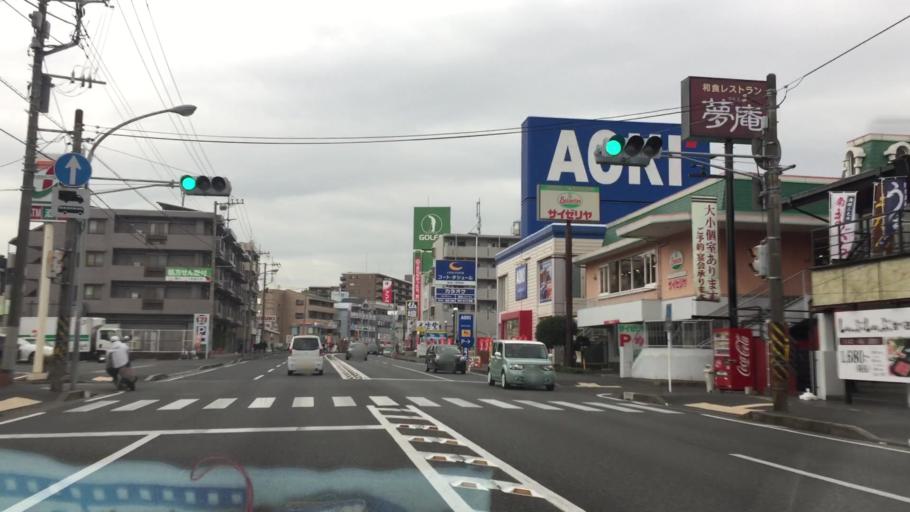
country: JP
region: Kanagawa
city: Zushi
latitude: 35.3443
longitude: 139.6144
